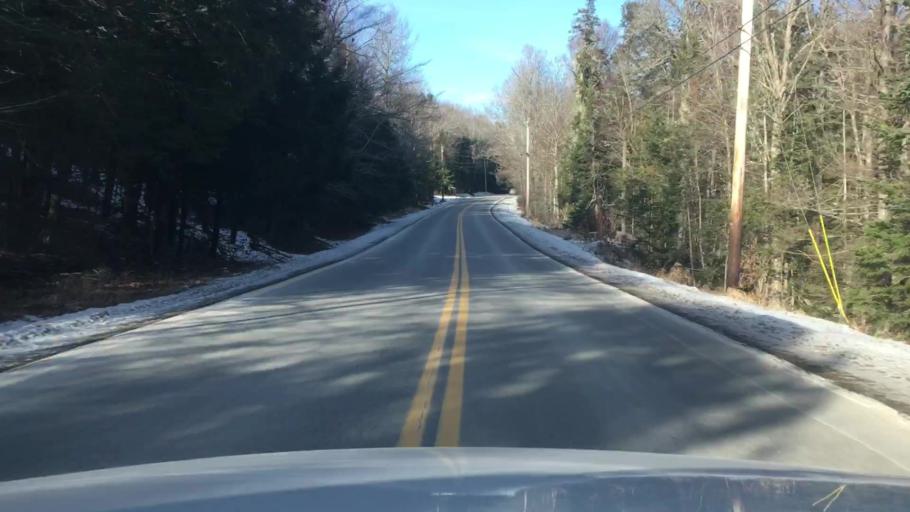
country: US
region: Maine
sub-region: Hancock County
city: Dedham
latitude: 44.6354
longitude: -68.6995
